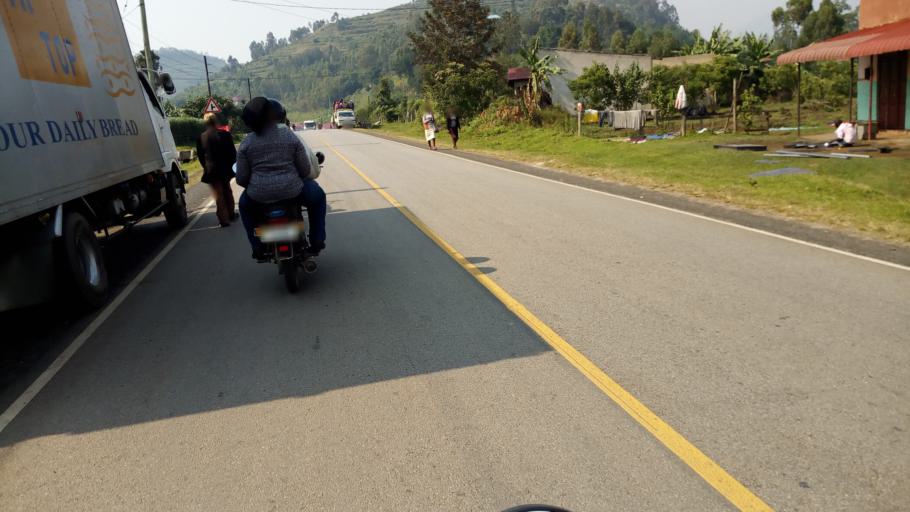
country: UG
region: Western Region
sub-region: Kisoro District
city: Kisoro
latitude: -1.2853
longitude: 29.7032
